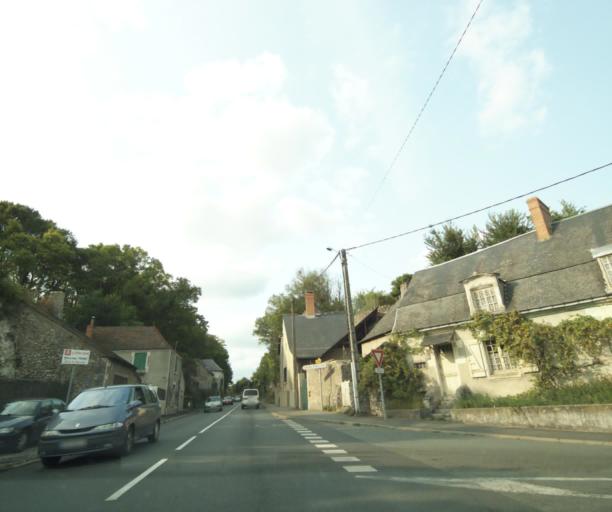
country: FR
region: Centre
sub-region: Departement d'Indre-et-Loire
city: Cormery
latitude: 47.2724
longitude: 0.8335
